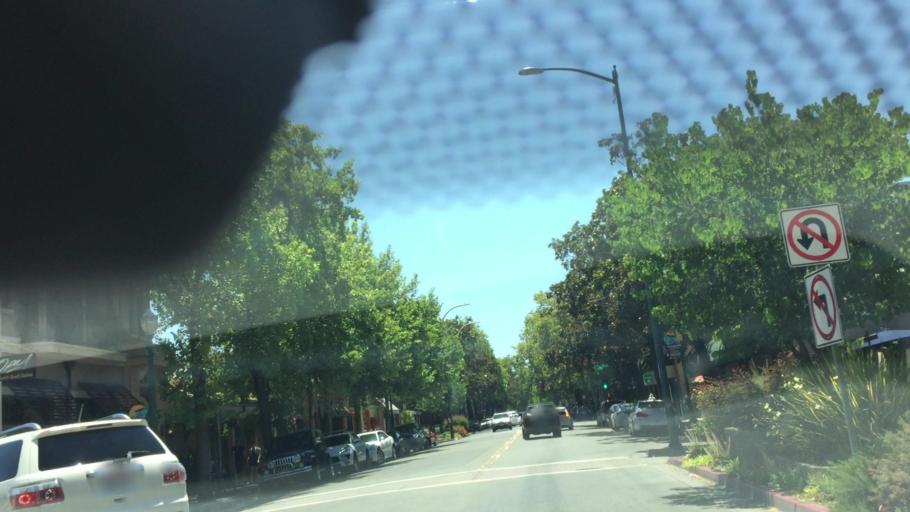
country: US
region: California
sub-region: Contra Costa County
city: Walnut Creek
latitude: 37.9007
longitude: -122.0614
